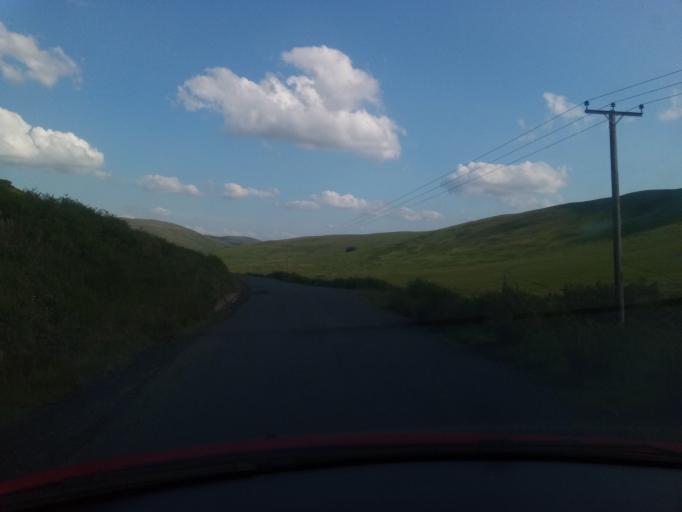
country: GB
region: Scotland
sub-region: The Scottish Borders
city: Innerleithen
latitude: 55.4649
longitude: -3.1273
